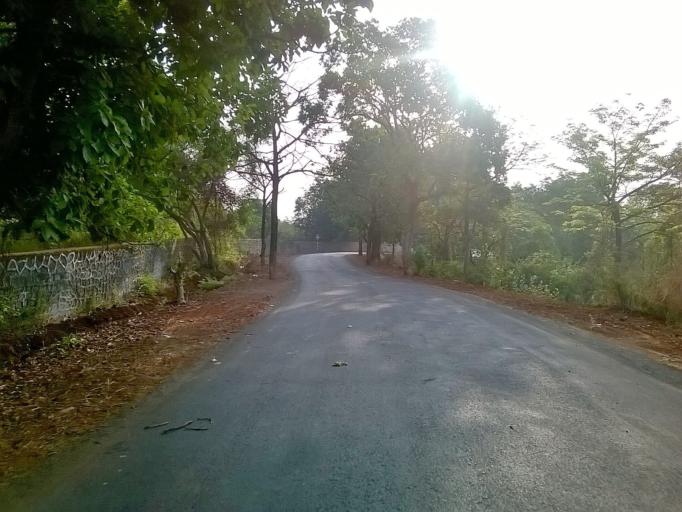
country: IN
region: Maharashtra
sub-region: Raigarh
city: Matheran
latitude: 19.0242
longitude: 73.2041
